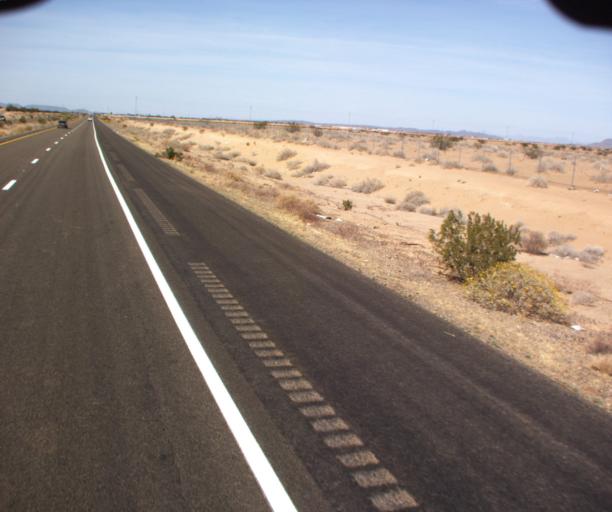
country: US
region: Arizona
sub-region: Yuma County
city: Fortuna Foothills
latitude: 32.6376
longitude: -114.5213
